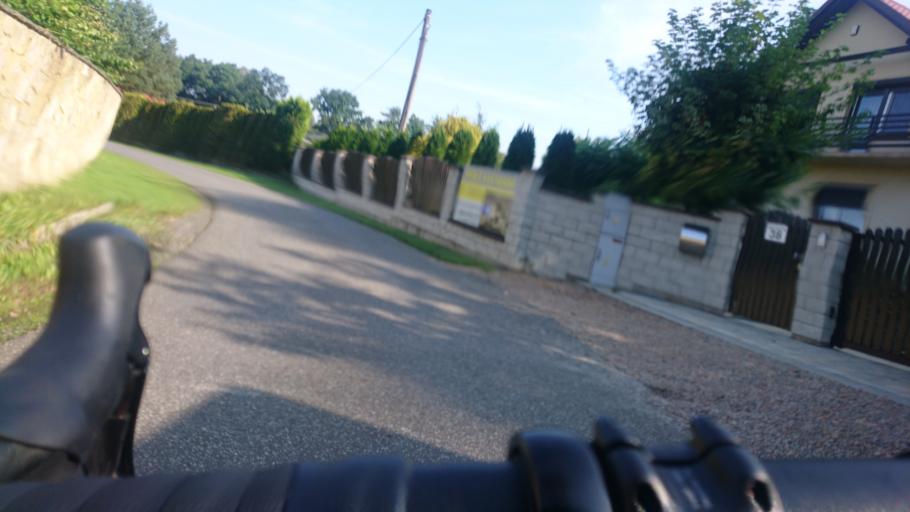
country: PL
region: Lesser Poland Voivodeship
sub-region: Powiat wadowicki
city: Sosnowice
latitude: 49.9557
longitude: 19.7080
